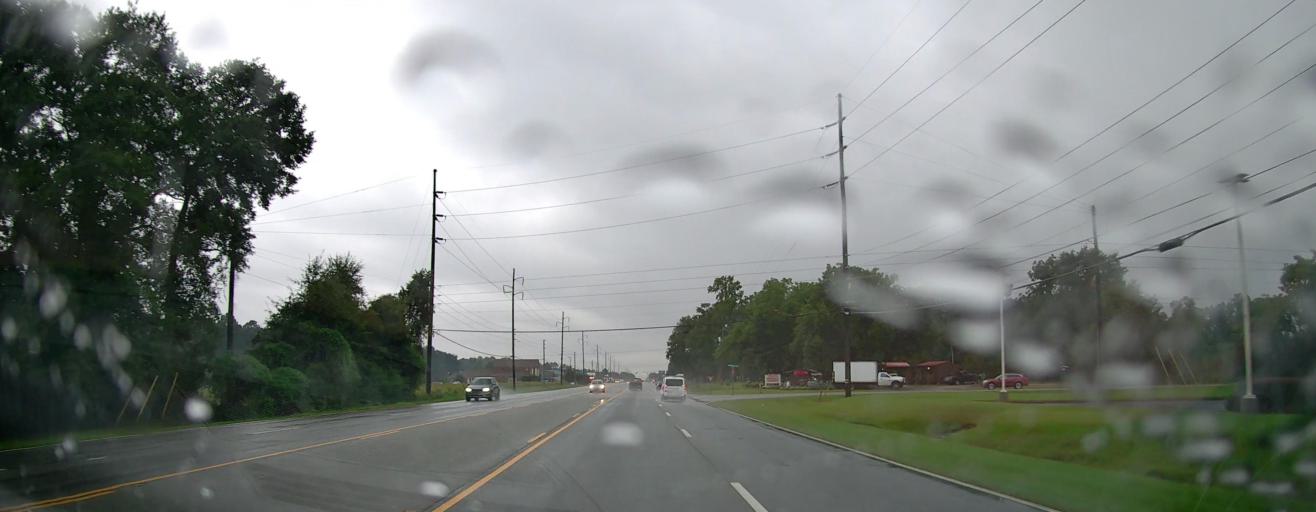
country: US
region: Georgia
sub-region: Houston County
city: Centerville
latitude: 32.6087
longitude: -83.6772
